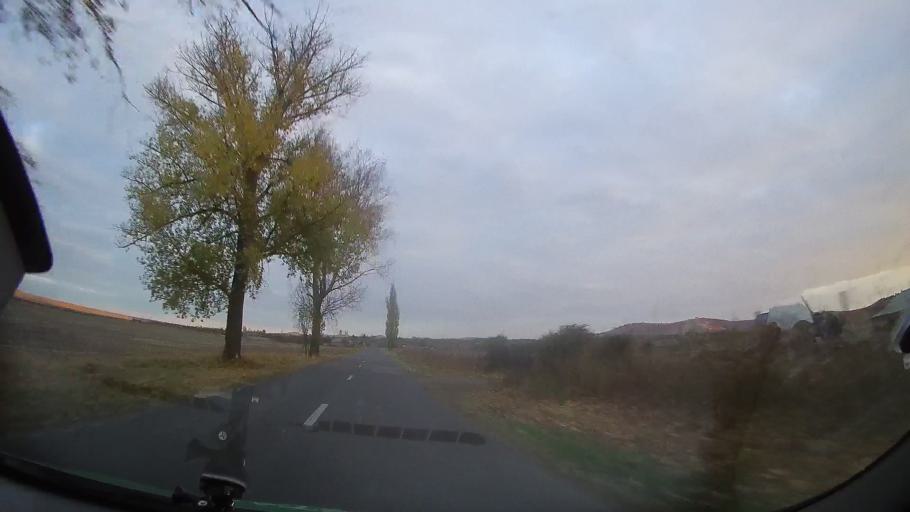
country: RO
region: Tulcea
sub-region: Comuna Mihai Bravu
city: Turda
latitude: 44.9841
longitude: 28.6128
